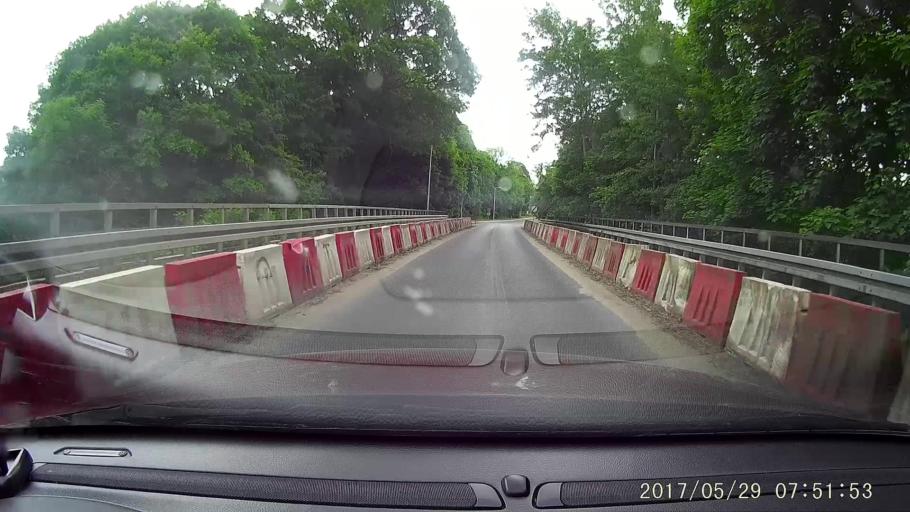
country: PL
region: Lower Silesian Voivodeship
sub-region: Powiat zlotoryjski
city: Olszanica
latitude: 51.2177
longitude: 15.7129
